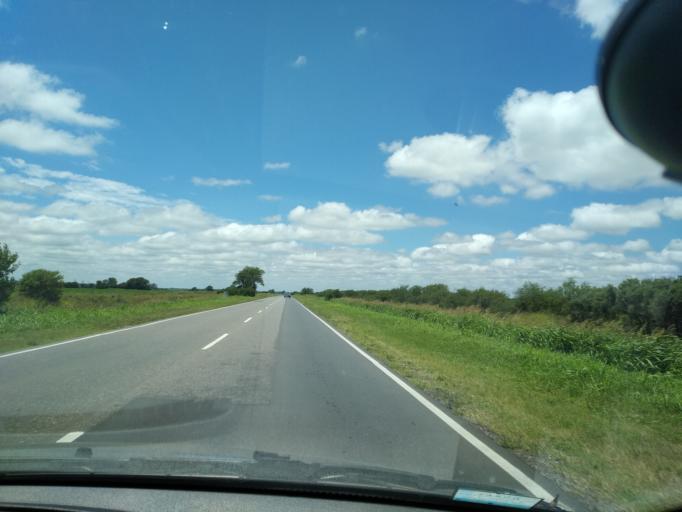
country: AR
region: Cordoba
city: Despenaderos
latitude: -31.6518
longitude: -64.2055
